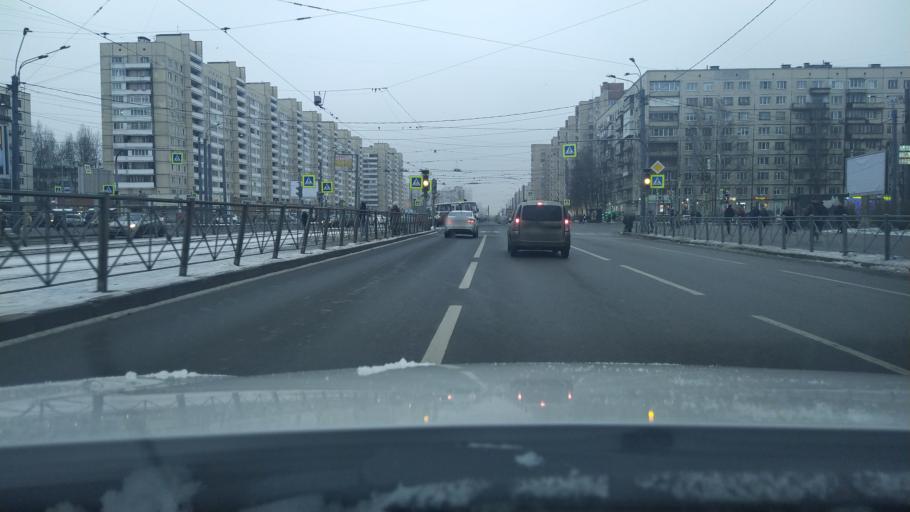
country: RU
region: St.-Petersburg
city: Grazhdanka
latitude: 60.0396
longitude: 30.4004
